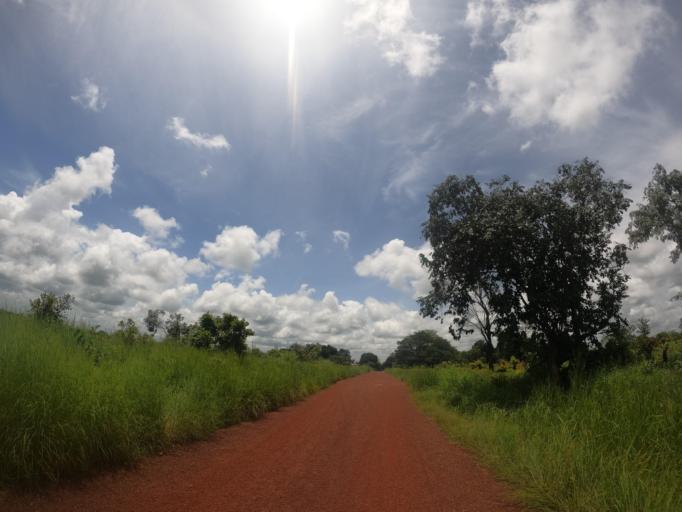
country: SL
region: Northern Province
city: Makeni
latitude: 9.1249
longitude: -12.2526
